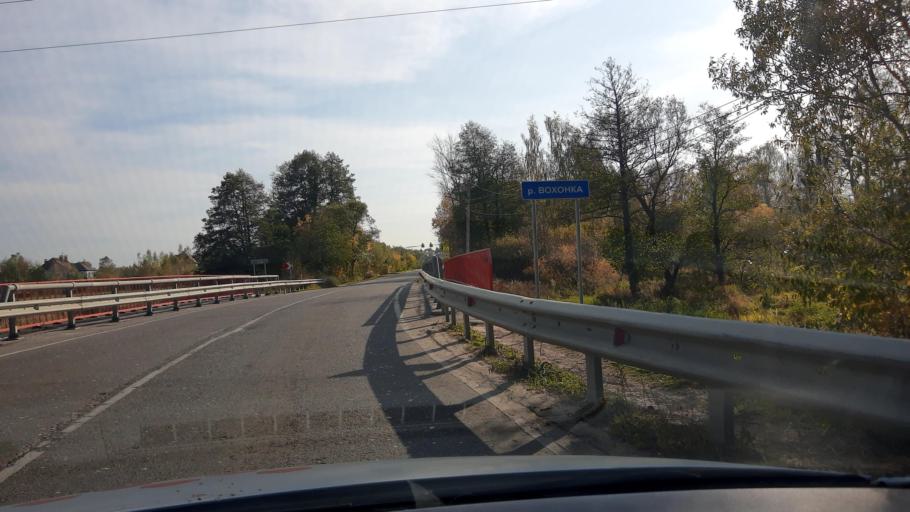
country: RU
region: Moskovskaya
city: Fryazevo
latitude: 55.7275
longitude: 38.4650
